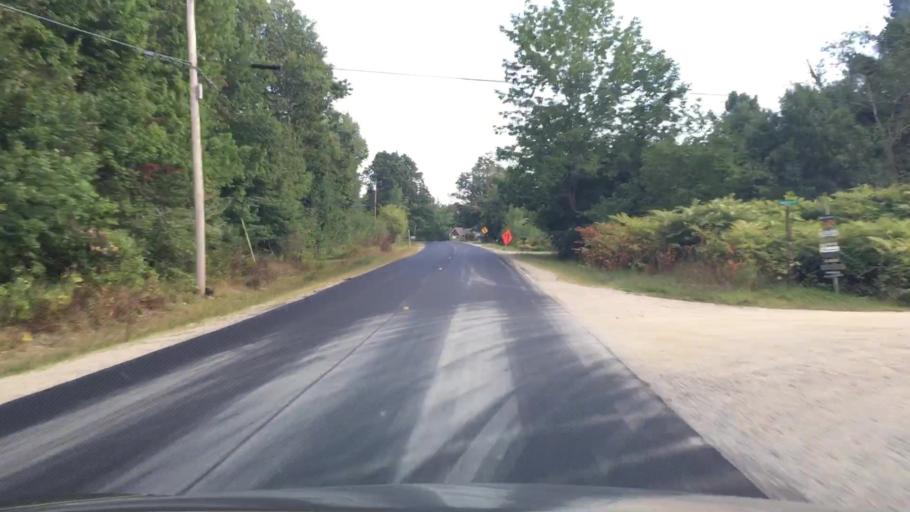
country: US
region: Maine
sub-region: Hancock County
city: Orland
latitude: 44.5477
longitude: -68.6206
